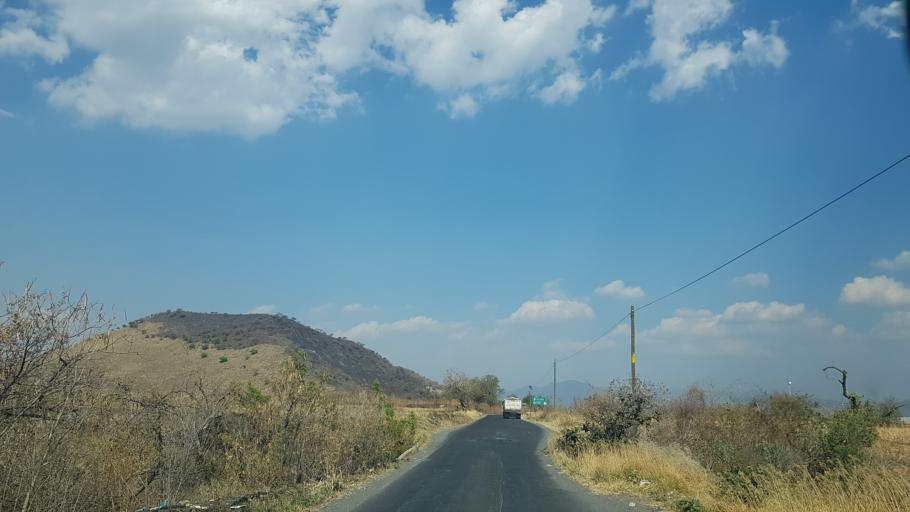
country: MX
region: Puebla
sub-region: Tianguismanalco
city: San Martin Tlapala
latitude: 18.9236
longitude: -98.4858
